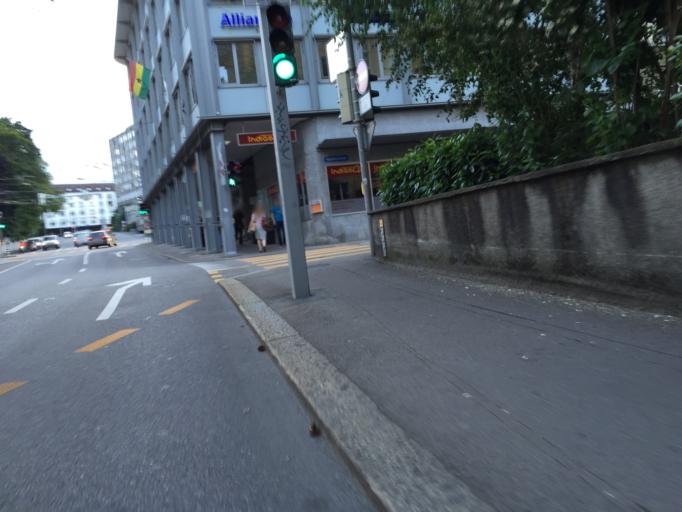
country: CH
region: Bern
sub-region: Bern-Mittelland District
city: Bern
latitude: 46.9453
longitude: 7.4332
